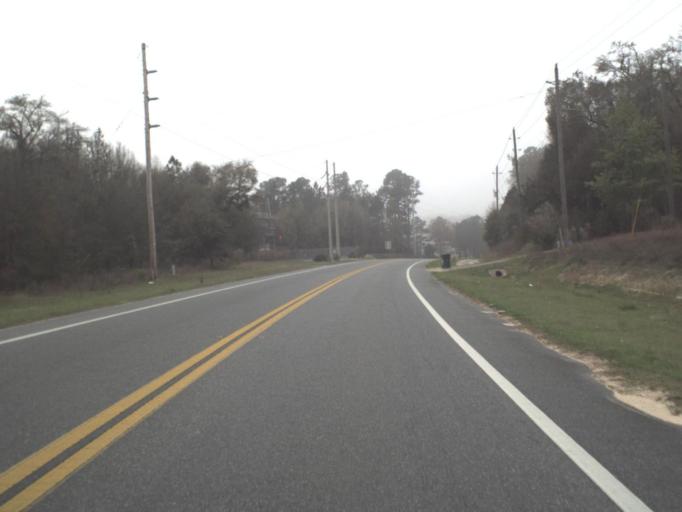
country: US
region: Florida
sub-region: Liberty County
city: Bristol
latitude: 30.3965
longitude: -84.7911
